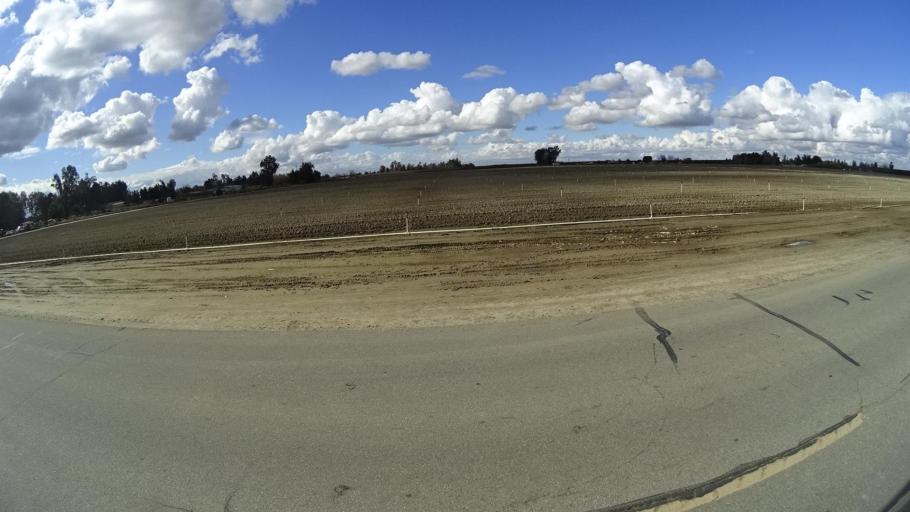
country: US
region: California
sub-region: Kern County
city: Greenfield
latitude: 35.2413
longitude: -119.0742
